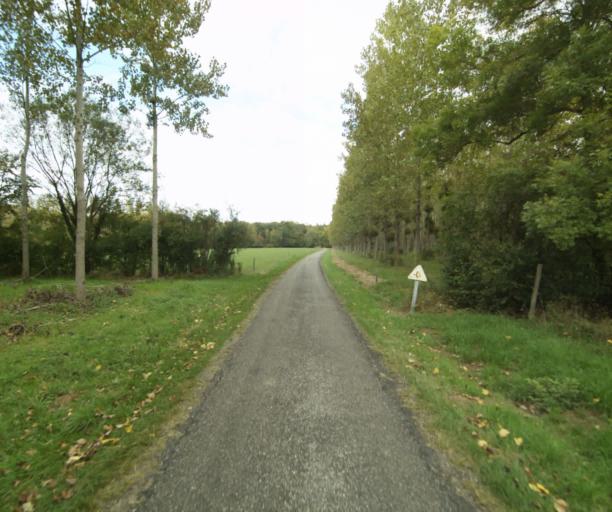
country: FR
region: Midi-Pyrenees
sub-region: Departement du Gers
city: Montreal
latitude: 43.9300
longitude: 0.1435
